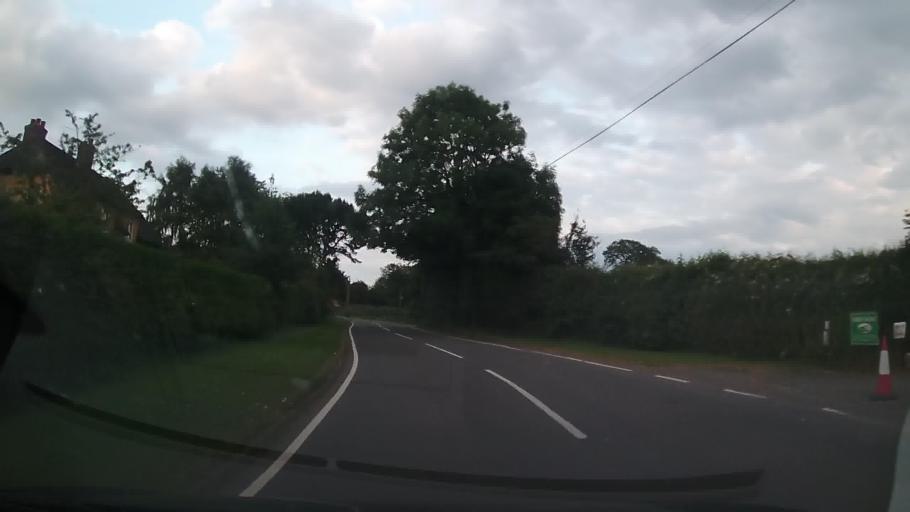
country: GB
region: England
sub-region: Shropshire
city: Petton
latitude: 52.8093
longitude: -2.8203
